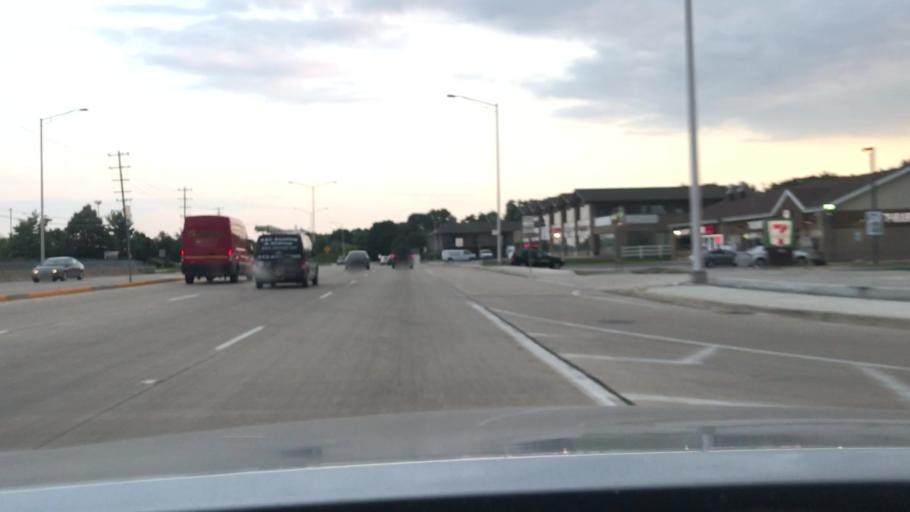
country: US
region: Illinois
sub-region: DuPage County
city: Warrenville
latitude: 41.7987
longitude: -88.2048
